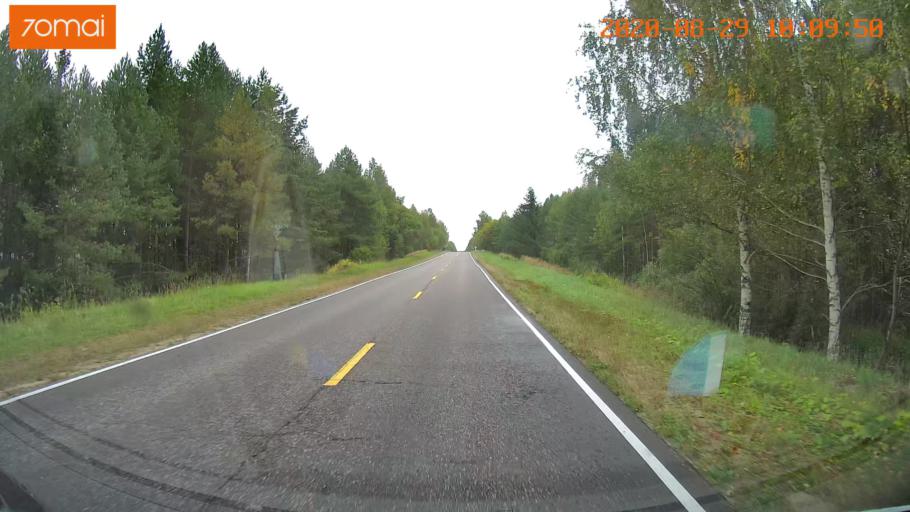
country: RU
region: Ivanovo
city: Kuznechikha
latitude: 57.3759
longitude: 42.6360
